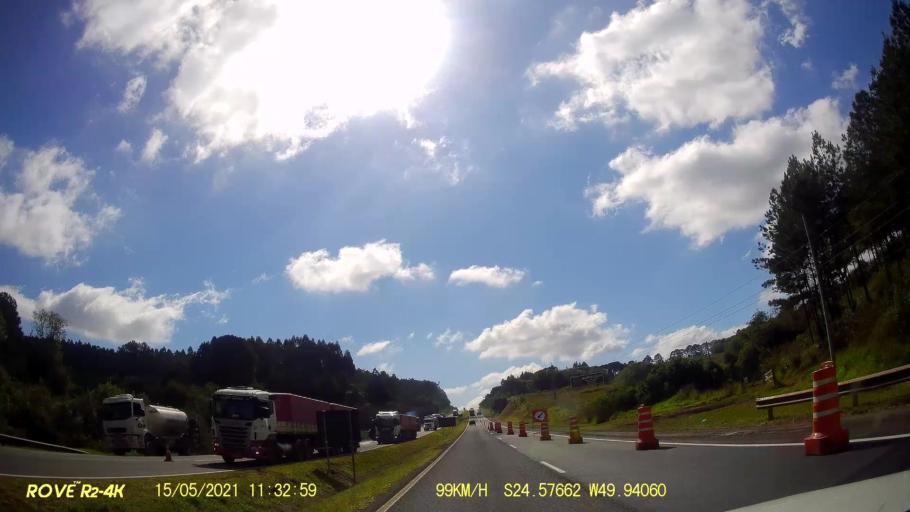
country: BR
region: Parana
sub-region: Pirai Do Sul
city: Pirai do Sul
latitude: -24.5767
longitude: -49.9406
